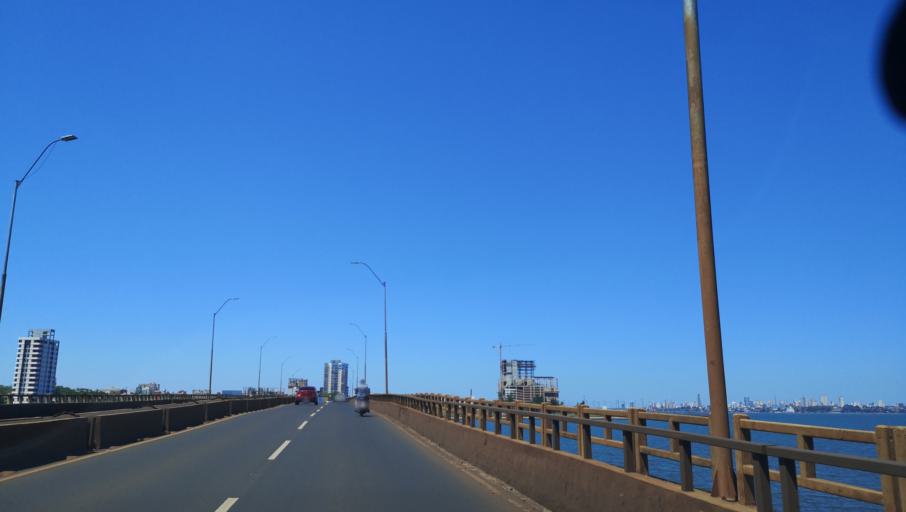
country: PY
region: Itapua
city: Encarnacion
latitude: -27.3173
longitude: -55.8750
